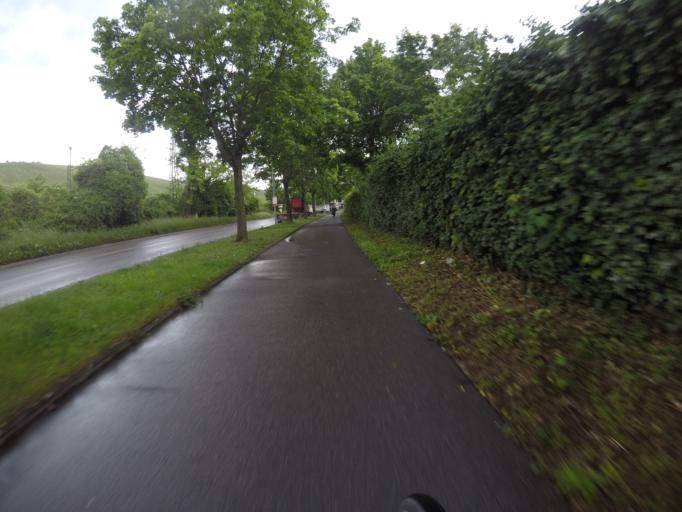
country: DE
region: Baden-Wuerttemberg
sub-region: Regierungsbezirk Stuttgart
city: Fellbach
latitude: 48.7760
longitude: 9.2555
